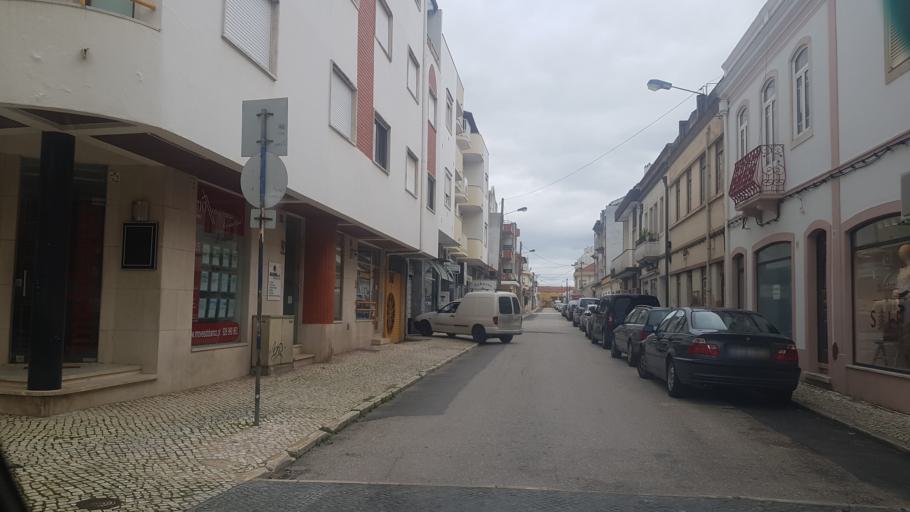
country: PT
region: Santarem
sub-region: Entroncamento
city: Entroncamento
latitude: 39.4639
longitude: -8.4689
